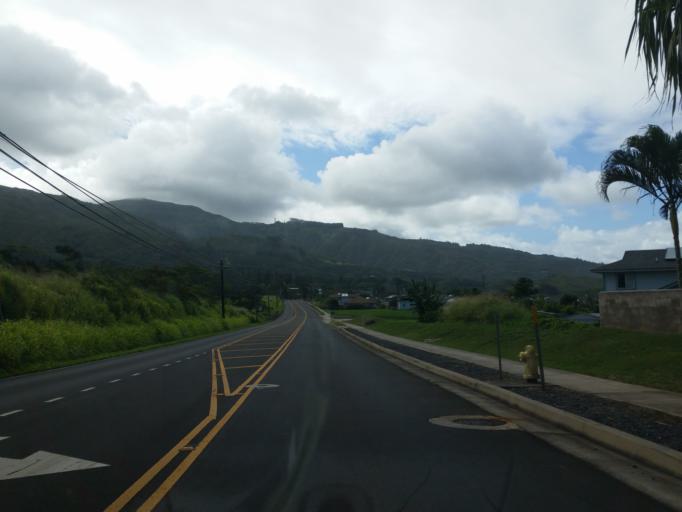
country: US
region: Hawaii
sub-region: Maui County
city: Waihee-Waiehu
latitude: 20.9260
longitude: -156.5055
